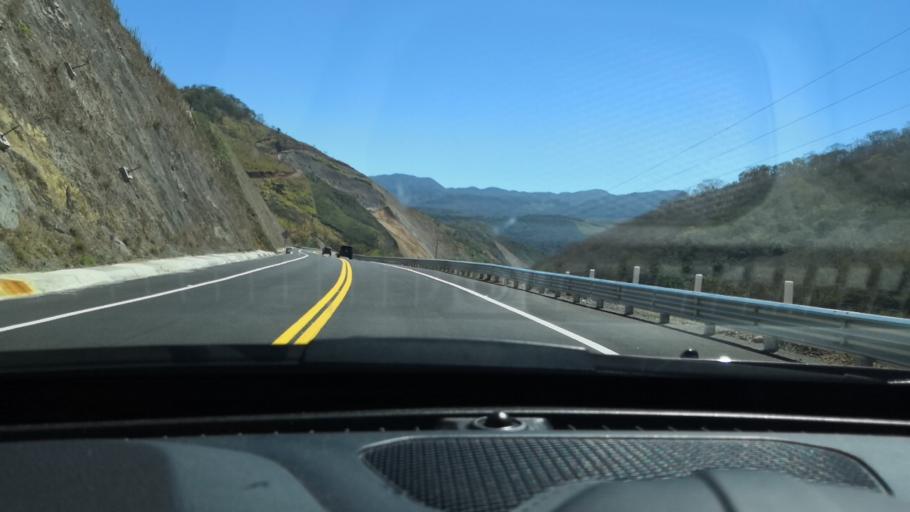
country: MX
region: Nayarit
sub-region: Compostela
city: Juan Escutia (Borbollon)
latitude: 21.1534
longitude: -104.9100
